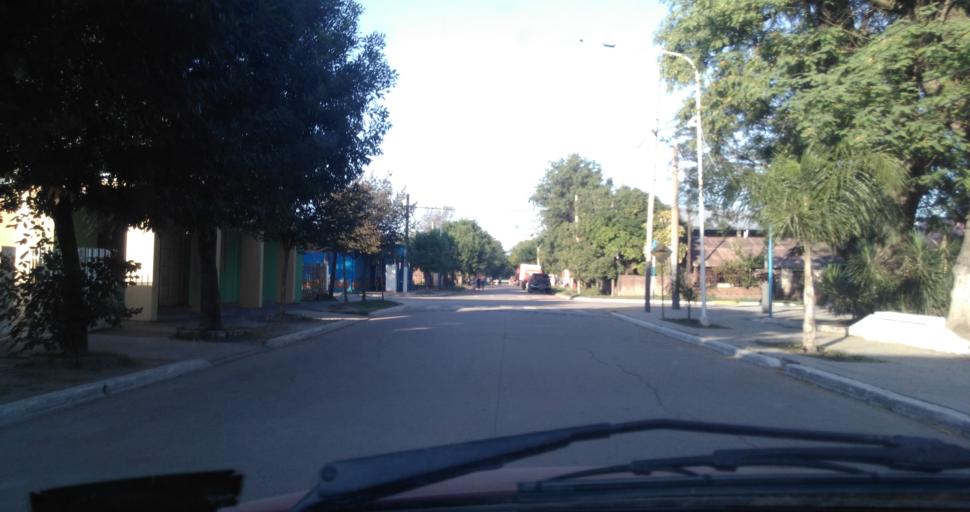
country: AR
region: Chaco
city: Fontana
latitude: -27.4161
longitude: -59.0343
